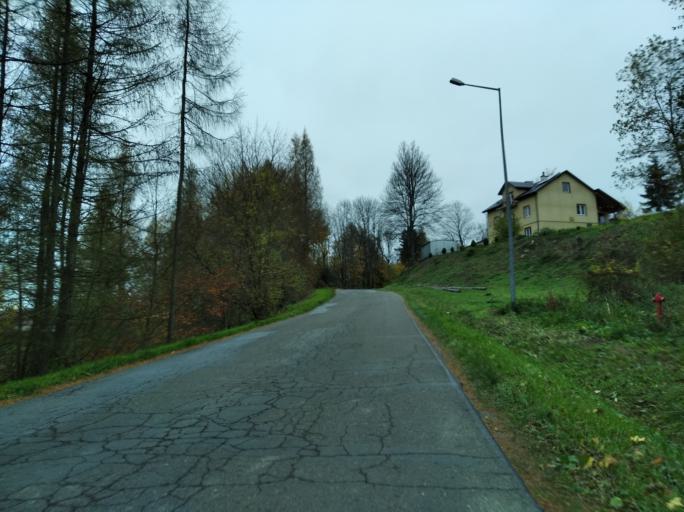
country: PL
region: Subcarpathian Voivodeship
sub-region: Powiat strzyzowski
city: Frysztak
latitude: 49.8356
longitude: 21.6244
